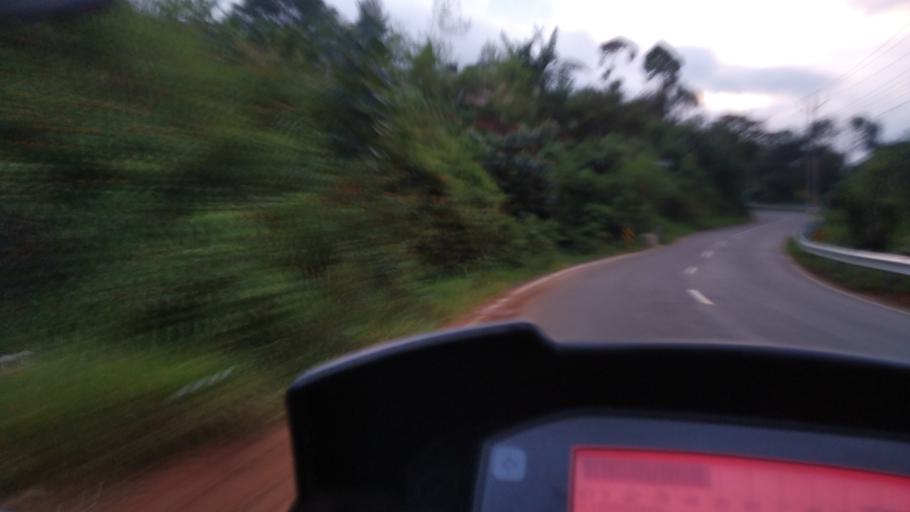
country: IN
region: Kerala
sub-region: Idukki
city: Munnar
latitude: 9.9688
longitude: 77.1271
